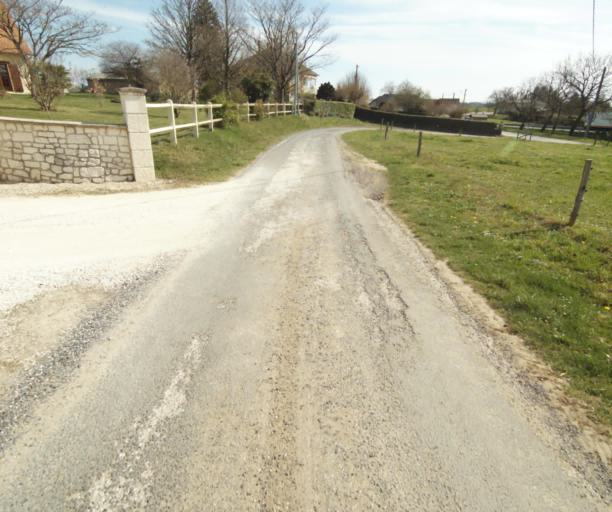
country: FR
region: Limousin
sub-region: Departement de la Correze
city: Seilhac
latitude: 45.3474
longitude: 1.7415
